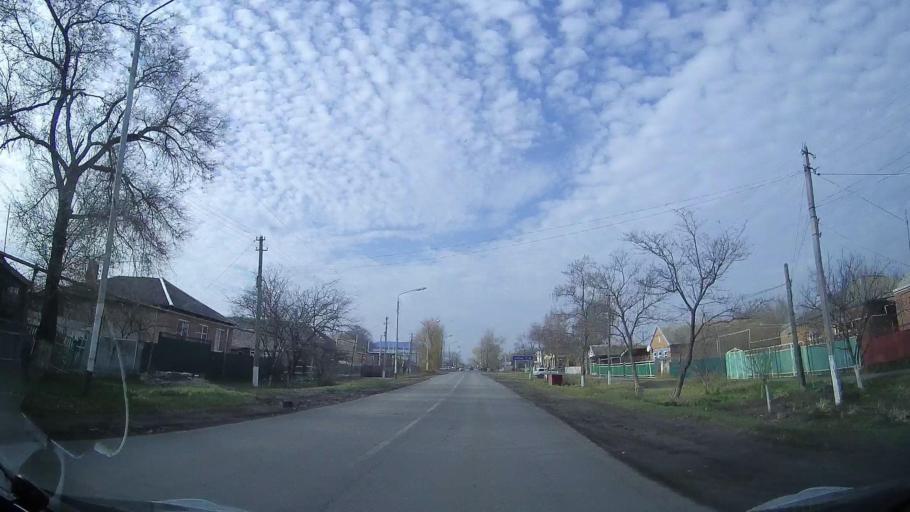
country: RU
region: Rostov
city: Veselyy
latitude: 47.0901
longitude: 40.7474
